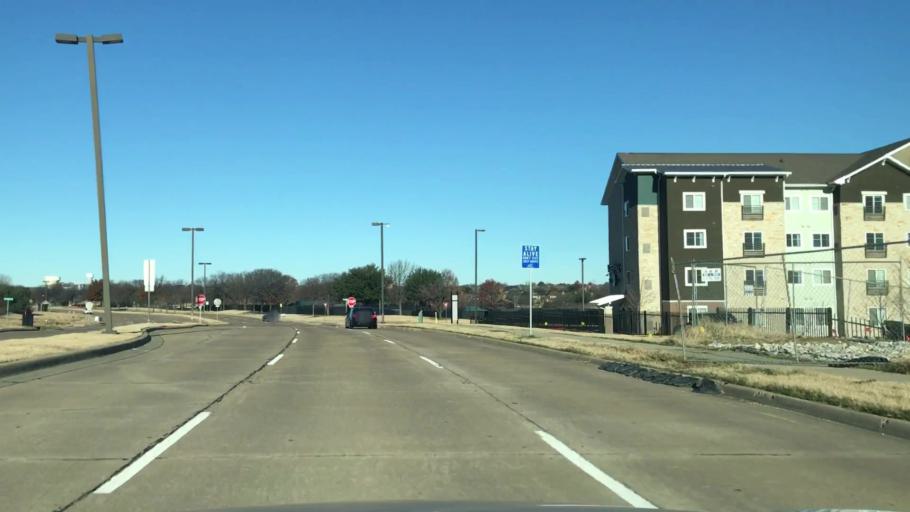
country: US
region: Texas
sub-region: Dallas County
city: Coppell
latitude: 32.9003
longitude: -96.9705
